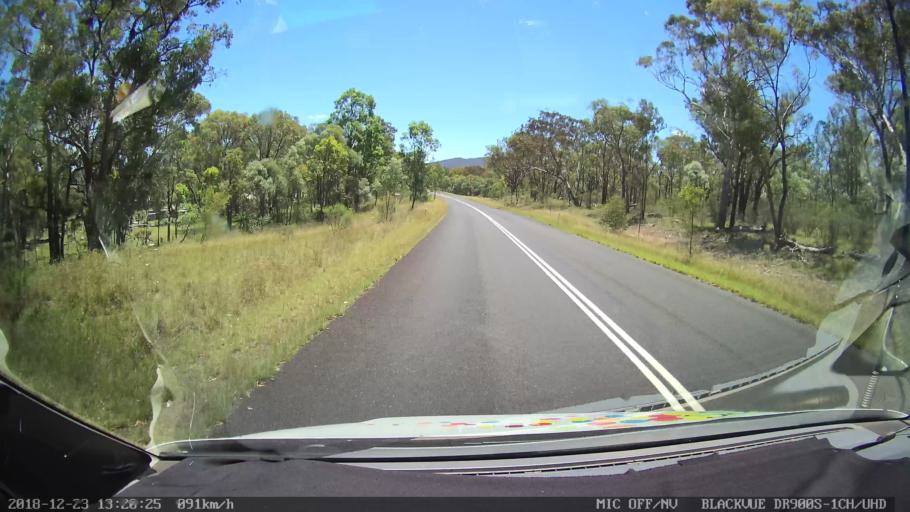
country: AU
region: New South Wales
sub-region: Armidale Dumaresq
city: Armidale
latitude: -30.4847
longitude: 151.4497
